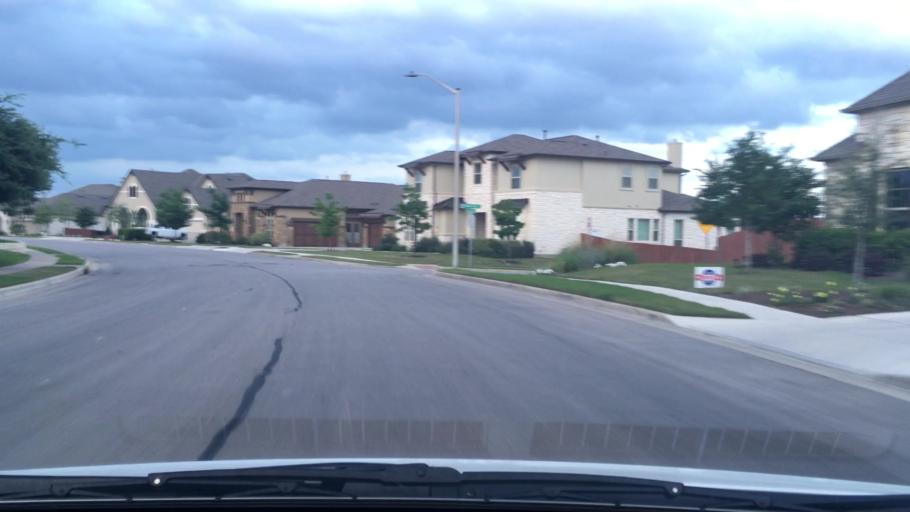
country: US
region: Texas
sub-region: Williamson County
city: Anderson Mill
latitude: 30.4541
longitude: -97.8566
